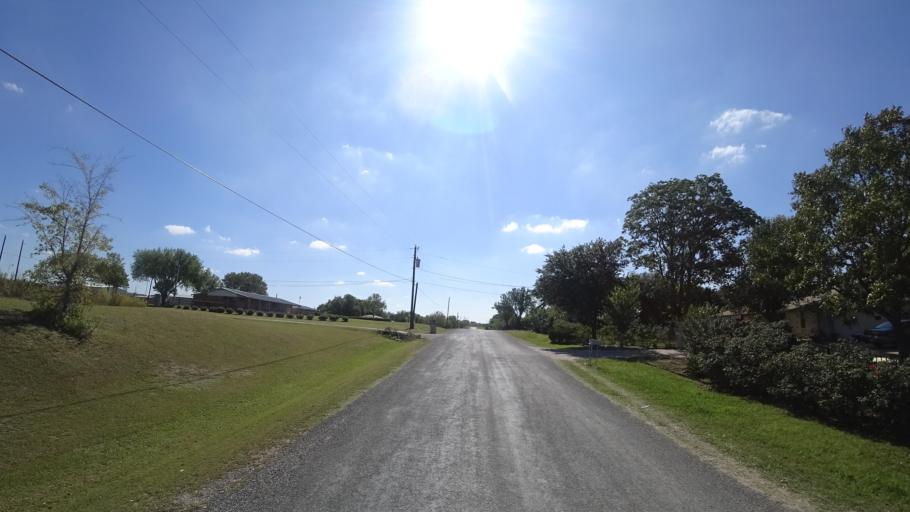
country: US
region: Texas
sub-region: Travis County
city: Manor
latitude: 30.3441
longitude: -97.6073
